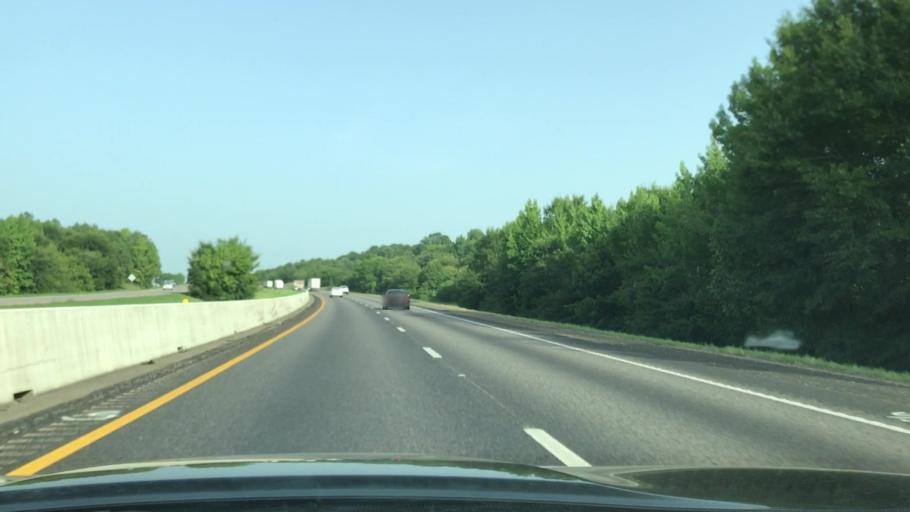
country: US
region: Texas
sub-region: Smith County
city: Lindale
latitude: 32.4677
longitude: -95.3415
